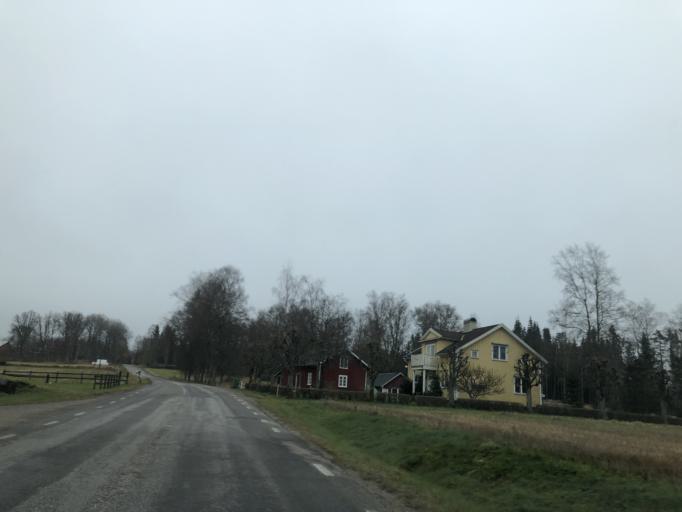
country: SE
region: Vaestra Goetaland
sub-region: Ulricehamns Kommun
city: Ulricehamn
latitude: 57.6930
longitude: 13.4886
